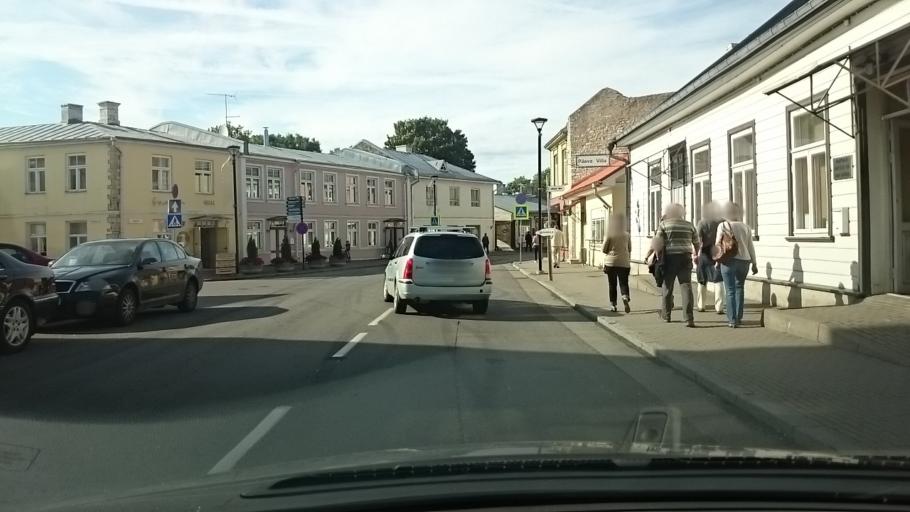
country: EE
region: Laeaene
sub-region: Haapsalu linn
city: Haapsalu
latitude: 58.9464
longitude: 23.5364
